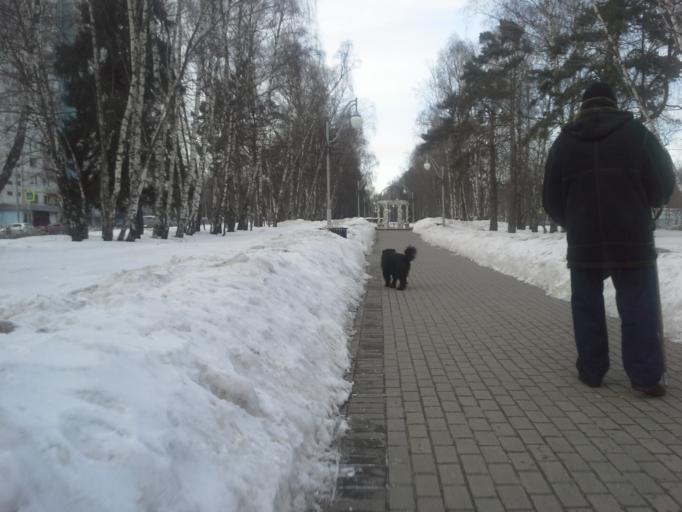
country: RU
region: Moscow
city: Yasenevo
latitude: 55.5922
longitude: 37.5467
